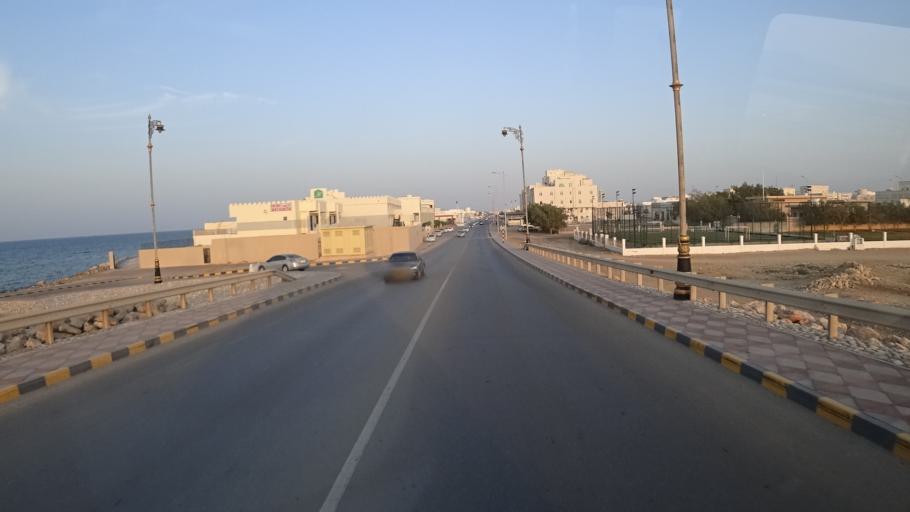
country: OM
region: Ash Sharqiyah
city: Sur
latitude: 22.5963
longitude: 59.4912
